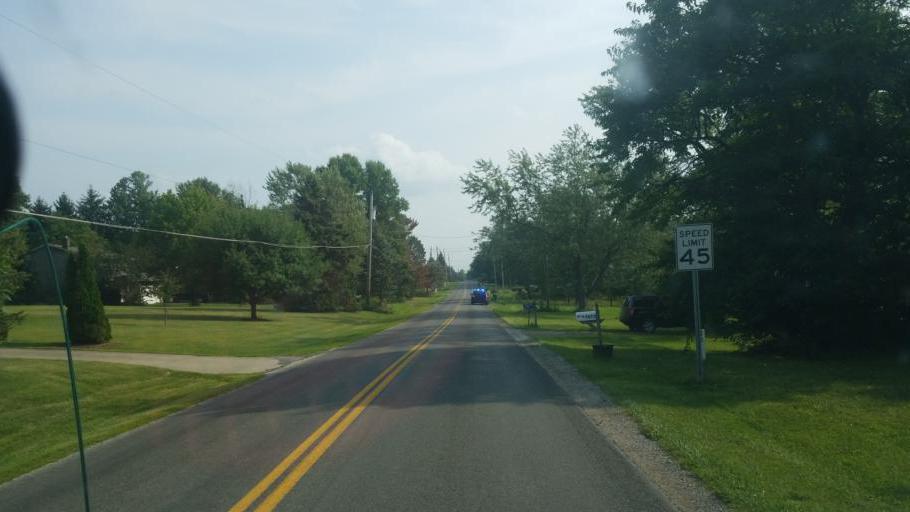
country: US
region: Ohio
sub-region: Medina County
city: Medina
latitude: 41.0809
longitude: -81.8849
